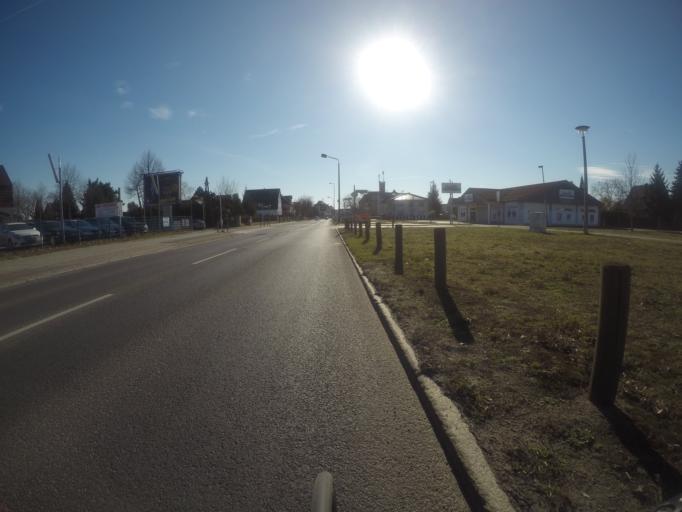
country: DE
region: Berlin
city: Biesdorf
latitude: 52.4894
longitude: 13.5754
